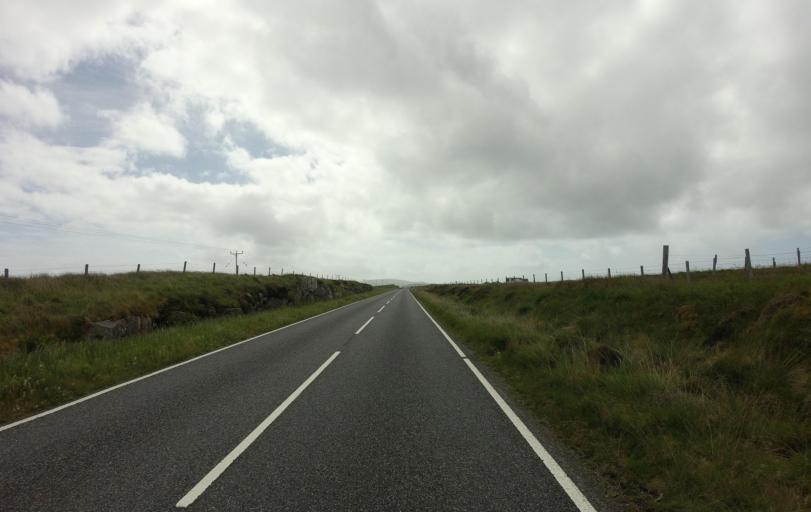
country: GB
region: Scotland
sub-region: Eilean Siar
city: Isle of South Uist
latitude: 57.1832
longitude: -7.3820
